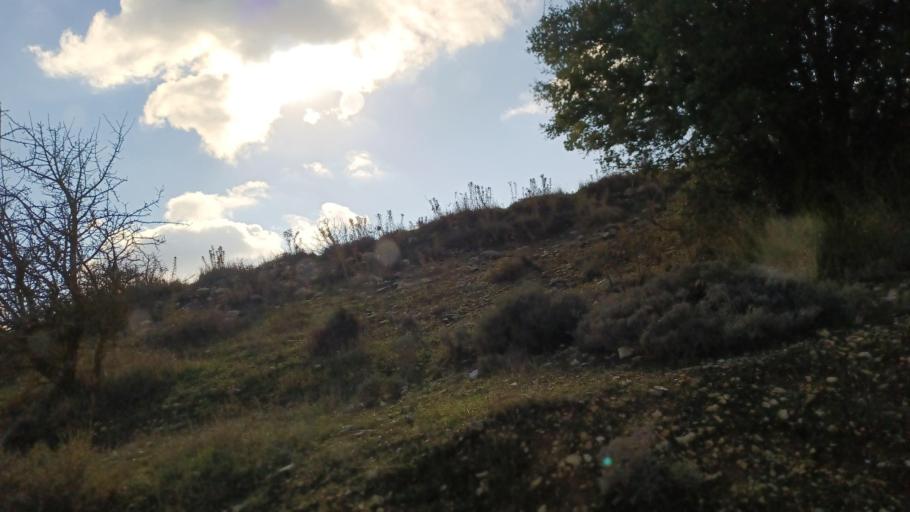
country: CY
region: Limassol
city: Pachna
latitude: 34.8468
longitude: 32.6833
